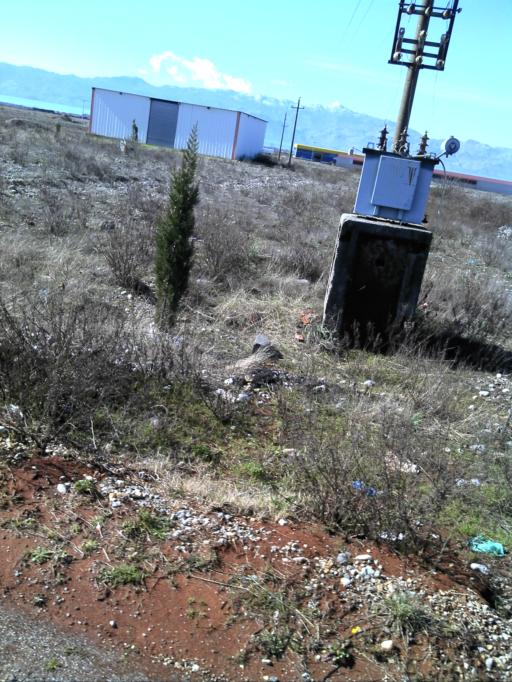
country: AL
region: Shkoder
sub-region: Rrethi i Malesia e Madhe
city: Koplik
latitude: 42.2311
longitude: 19.4245
